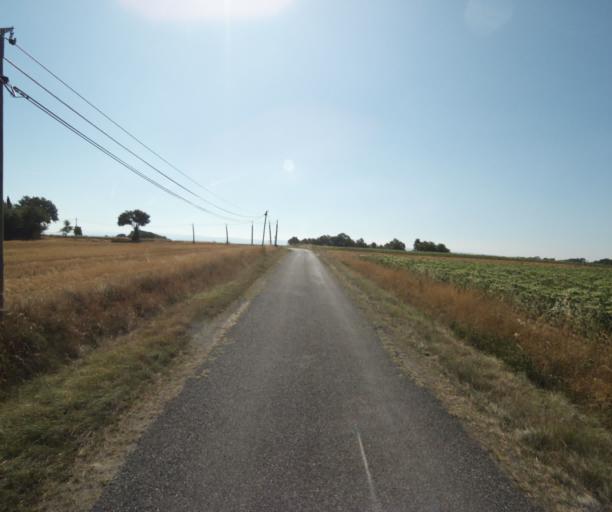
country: FR
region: Midi-Pyrenees
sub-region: Departement de la Haute-Garonne
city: Saint-Felix-Lauragais
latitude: 43.4897
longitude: 1.9174
